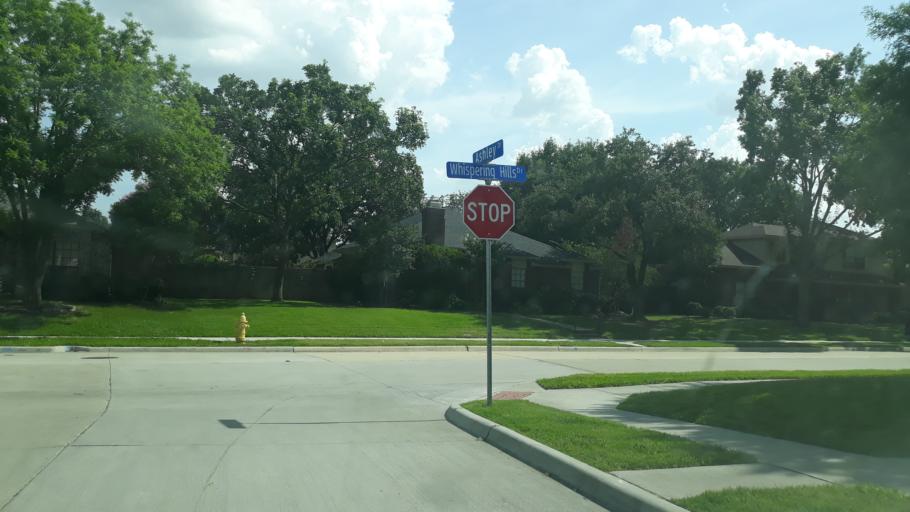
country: US
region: Texas
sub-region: Dallas County
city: Coppell
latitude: 32.9632
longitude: -97.0040
